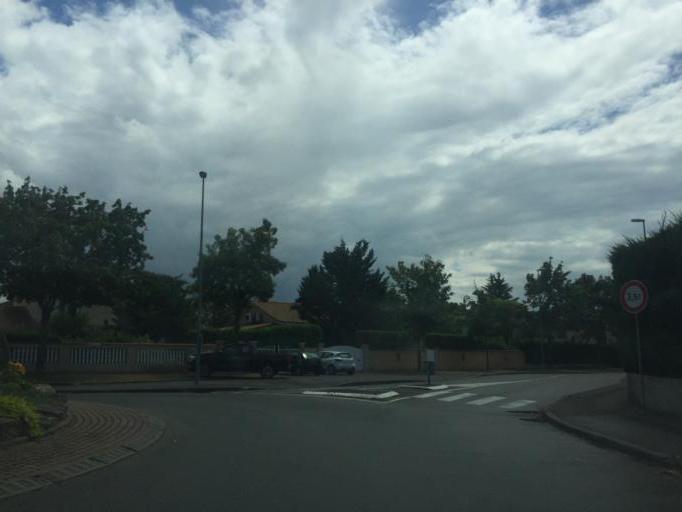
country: FR
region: Rhone-Alpes
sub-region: Departement de l'Isere
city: Janneyrias
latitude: 45.7948
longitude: 5.1223
